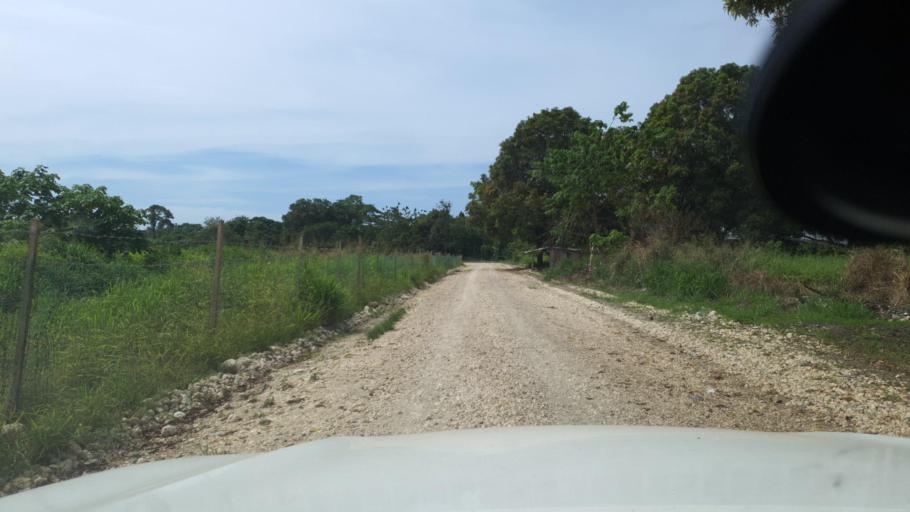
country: SB
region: Guadalcanal
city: Honiara
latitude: -9.4144
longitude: 159.8920
